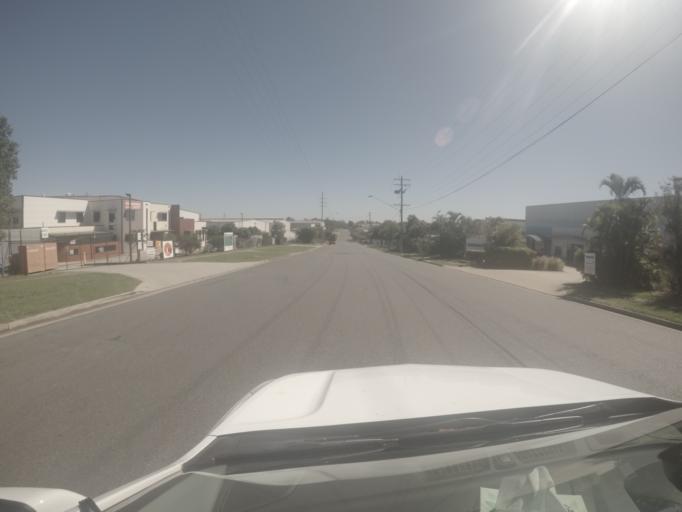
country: AU
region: Queensland
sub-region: Brisbane
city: Richlands
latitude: -27.5790
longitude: 152.9537
